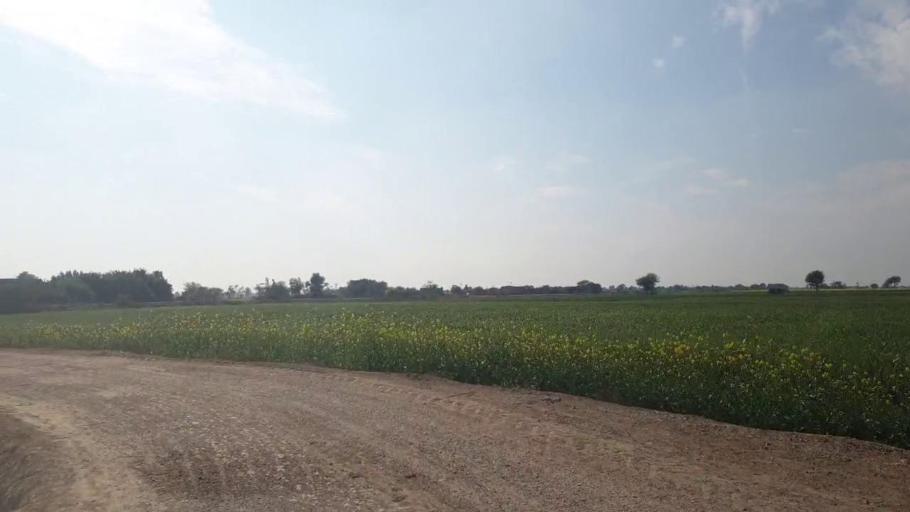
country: PK
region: Sindh
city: Shahdadpur
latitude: 25.9903
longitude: 68.5604
